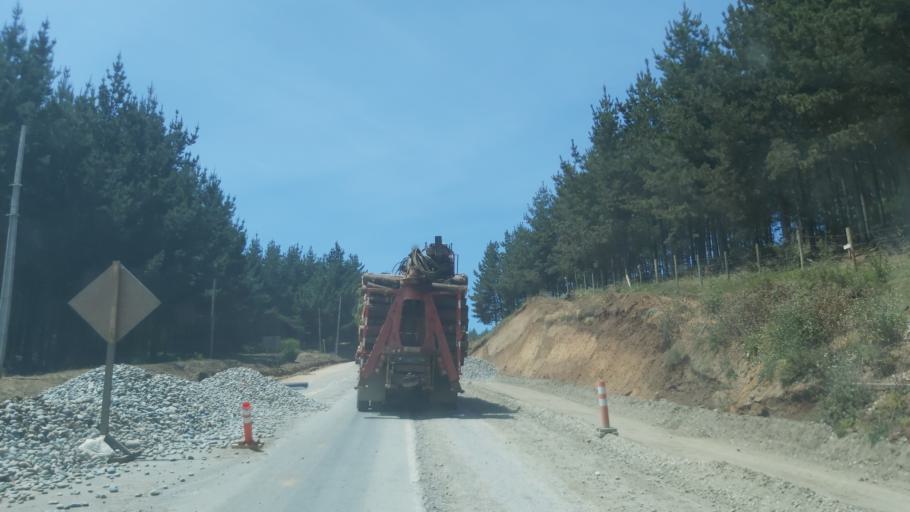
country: CL
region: Maule
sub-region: Provincia de Talca
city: Constitucion
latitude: -35.4496
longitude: -72.4767
